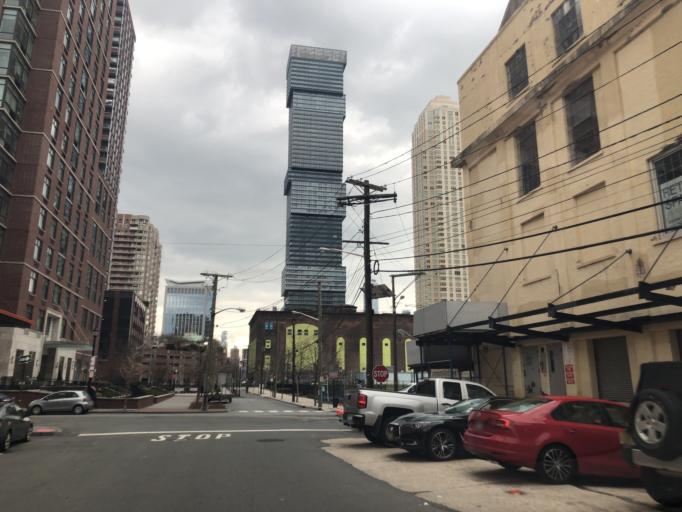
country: US
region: New Jersey
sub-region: Hudson County
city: Hoboken
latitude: 40.7212
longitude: -74.0387
